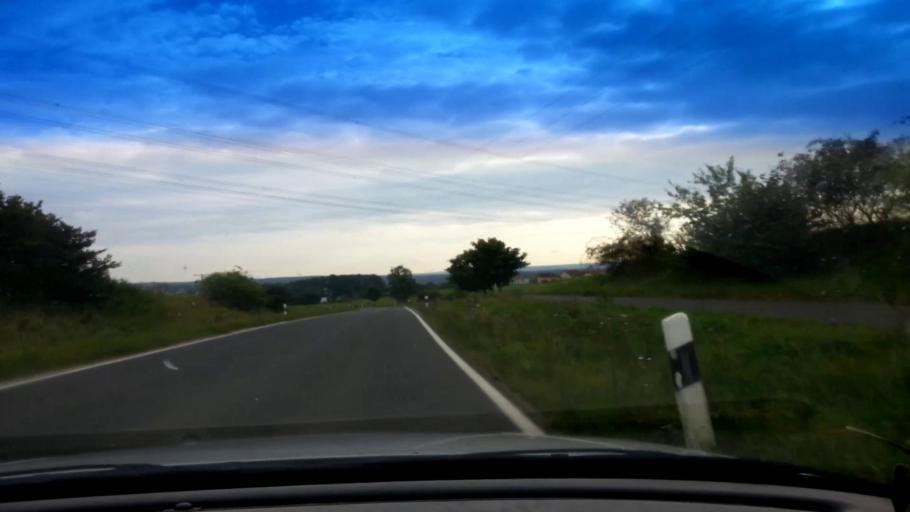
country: DE
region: Bavaria
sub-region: Upper Franconia
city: Memmelsdorf
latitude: 49.9484
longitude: 10.9558
